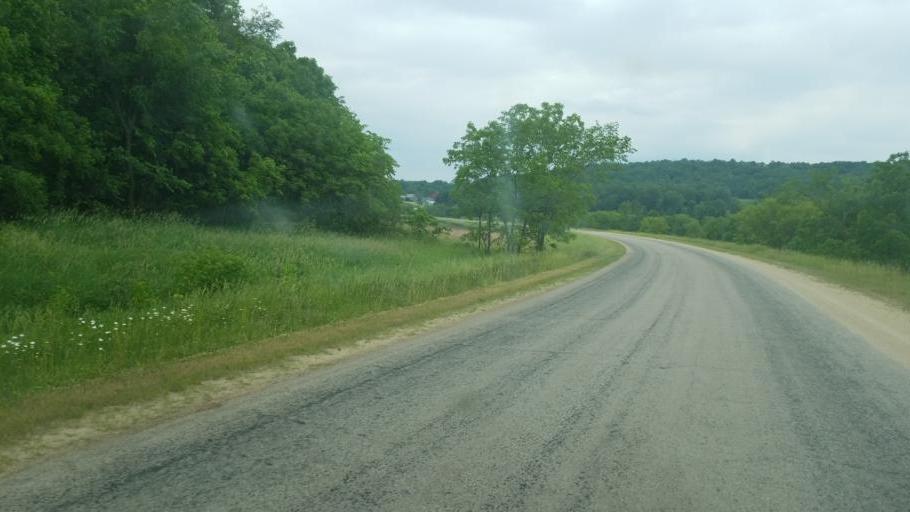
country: US
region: Wisconsin
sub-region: Vernon County
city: Hillsboro
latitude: 43.6122
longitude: -90.3590
